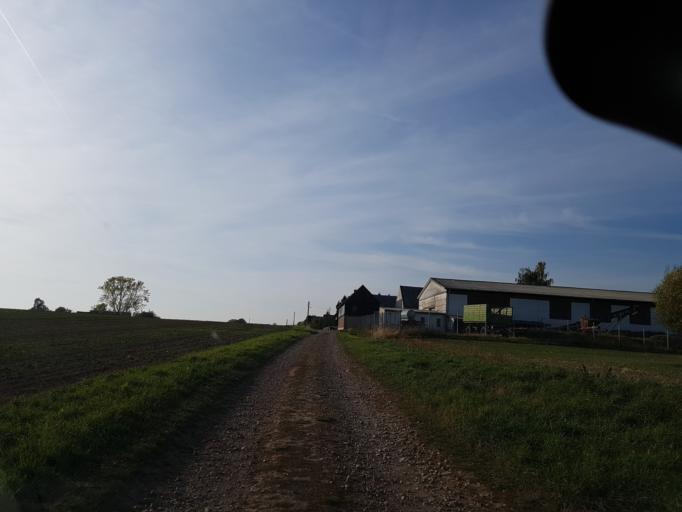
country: DE
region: Saxony
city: Waldheim
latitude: 51.0902
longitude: 13.0076
